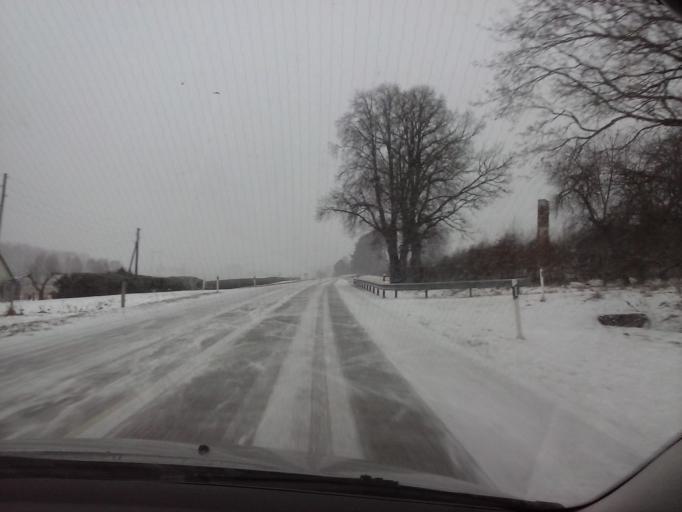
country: EE
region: Valgamaa
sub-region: Torva linn
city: Torva
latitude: 58.0363
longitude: 26.1820
